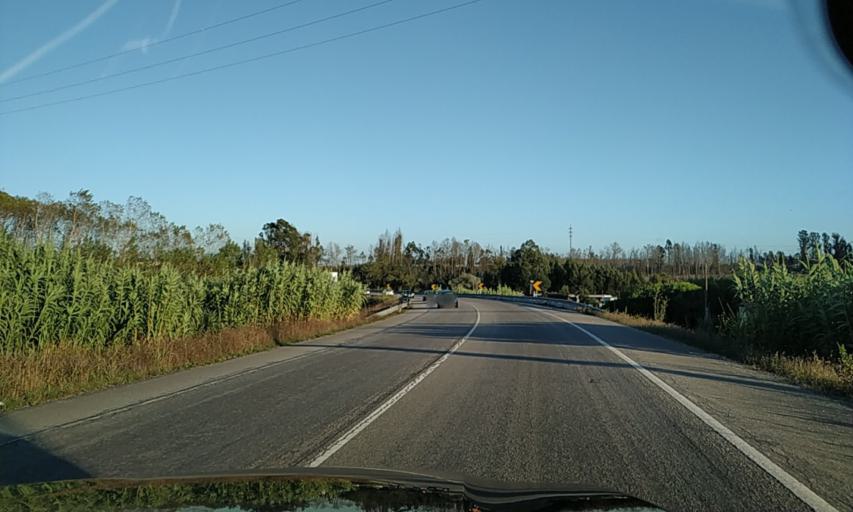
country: PT
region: Aveiro
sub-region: Aveiro
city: Oliveirinha
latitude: 40.5856
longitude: -8.6064
